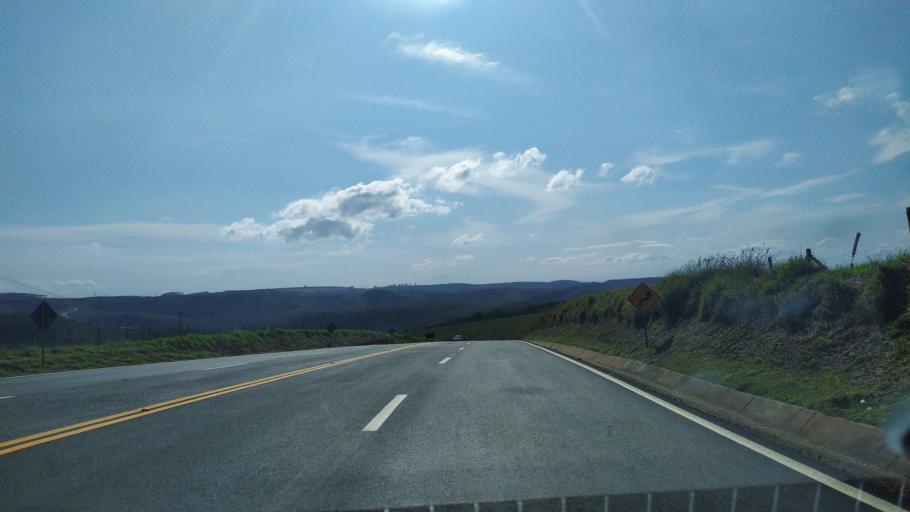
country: BR
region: Parana
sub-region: Telemaco Borba
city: Telemaco Borba
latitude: -24.2808
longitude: -50.7139
